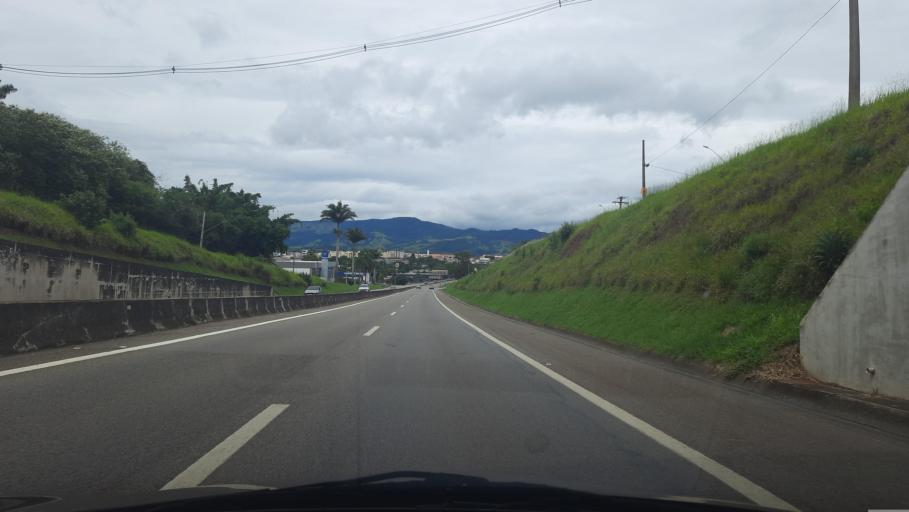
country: BR
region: Sao Paulo
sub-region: Sao Joao Da Boa Vista
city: Sao Joao da Boa Vista
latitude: -21.9854
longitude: -46.7886
